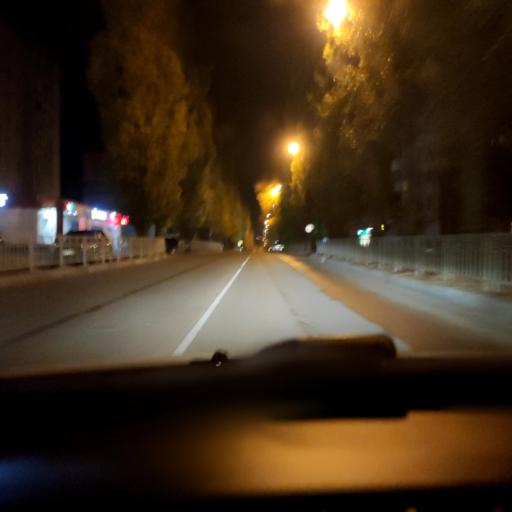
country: RU
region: Voronezj
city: Voronezh
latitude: 51.6875
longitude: 39.2588
